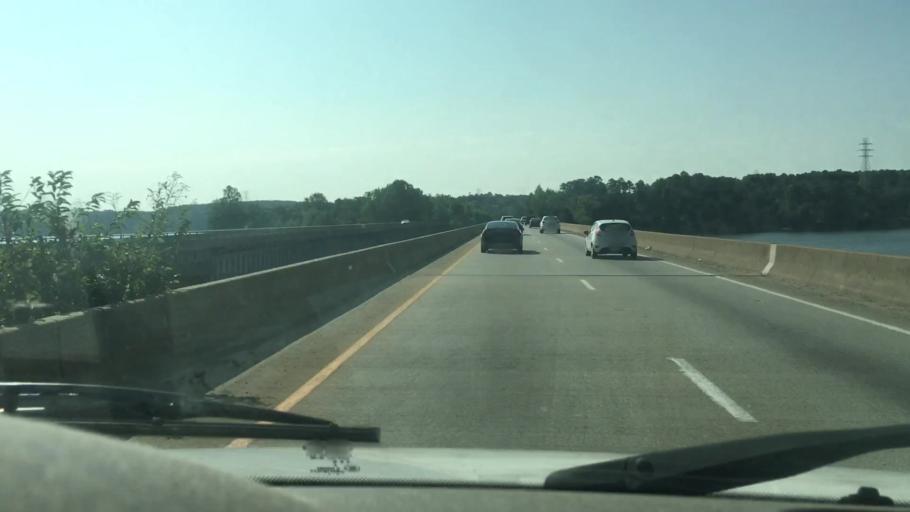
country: US
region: North Carolina
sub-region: Gaston County
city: Mount Holly
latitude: 35.3511
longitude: -80.9736
